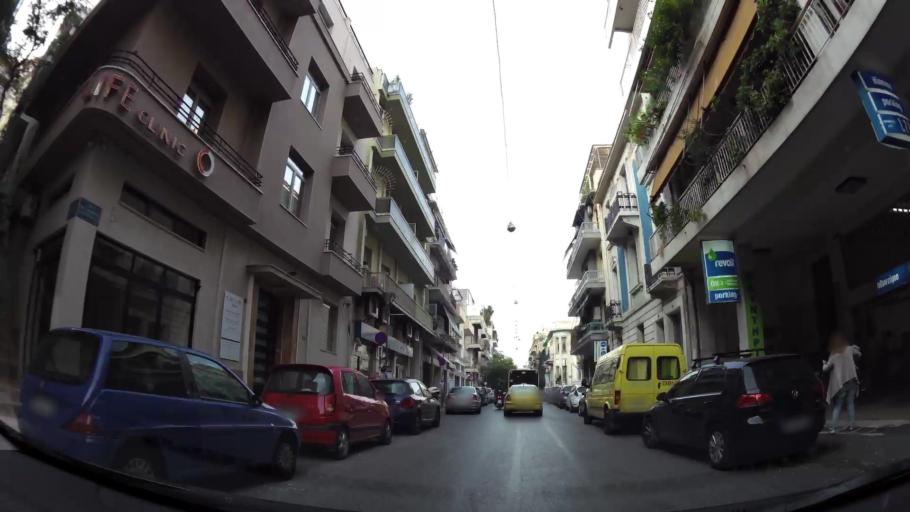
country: GR
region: Attica
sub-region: Nomarchia Athinas
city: Kipseli
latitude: 37.9875
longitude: 23.7453
